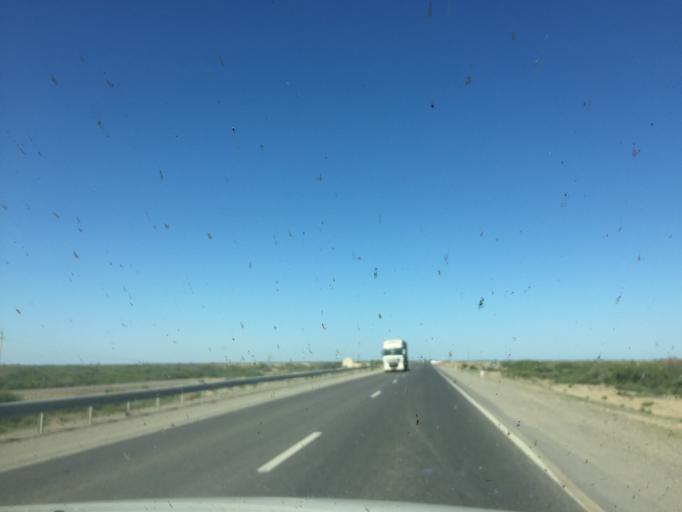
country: KZ
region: Qyzylorda
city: Terenozek
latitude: 44.8629
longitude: 64.8480
